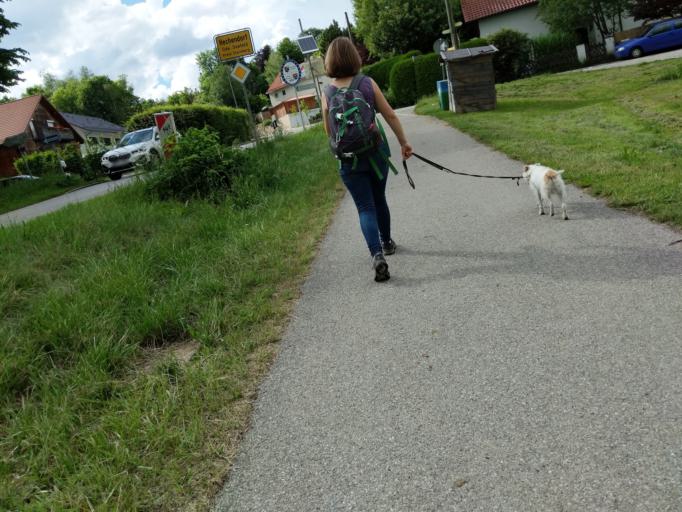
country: DE
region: Bavaria
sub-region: Upper Bavaria
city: Seefeld
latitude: 48.0385
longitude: 11.1980
